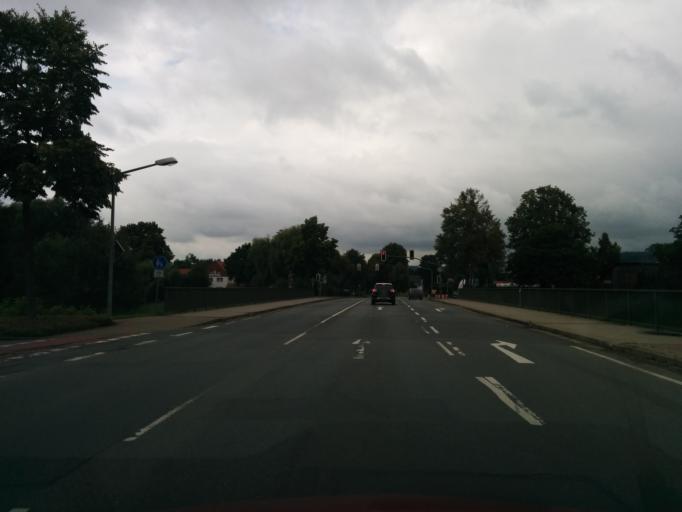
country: DE
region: Lower Saxony
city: Gieboldehausen
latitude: 51.6087
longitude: 10.2111
